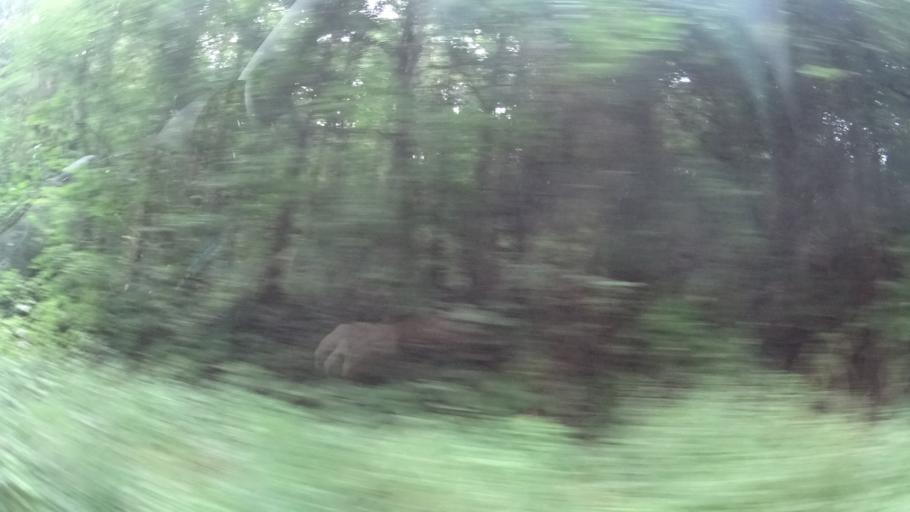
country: DE
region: Baden-Wuerttemberg
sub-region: Regierungsbezirk Stuttgart
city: Werbach
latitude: 49.7102
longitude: 9.6023
